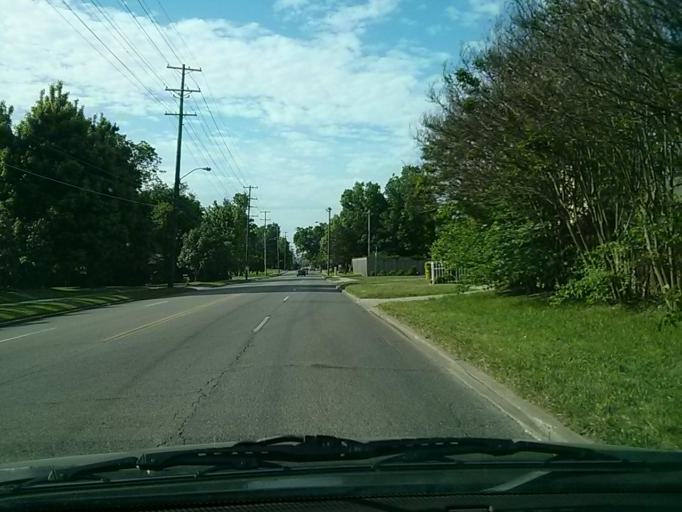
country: US
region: Oklahoma
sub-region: Tulsa County
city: Tulsa
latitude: 36.1226
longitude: -95.9757
